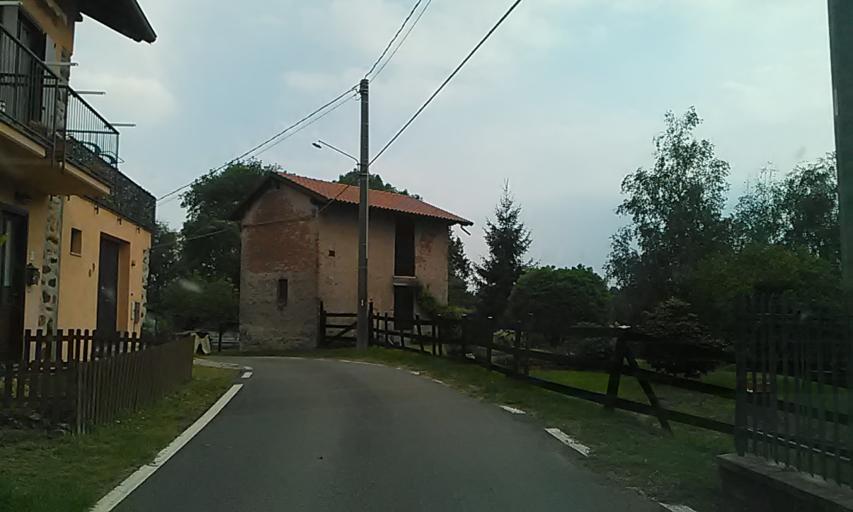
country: IT
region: Piedmont
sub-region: Provincia di Biella
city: Villa del Bosco
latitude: 45.6260
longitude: 8.2761
